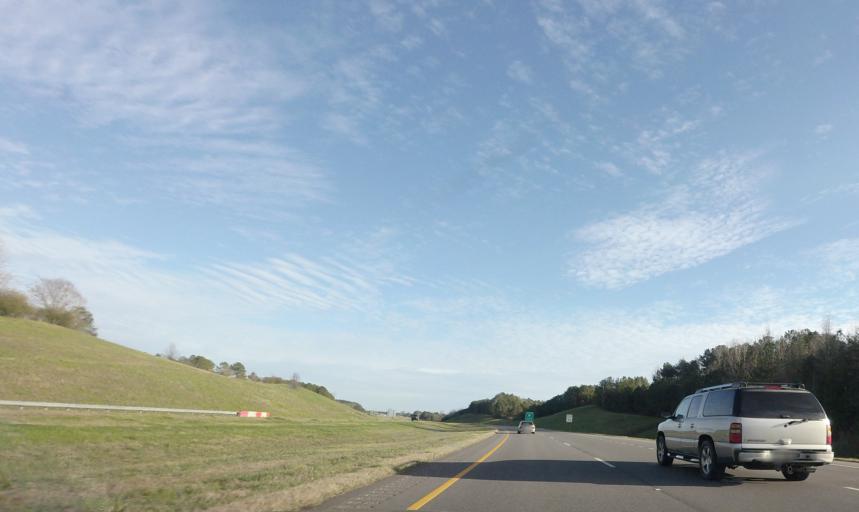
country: US
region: Alabama
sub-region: Walker County
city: Jasper
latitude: 33.8139
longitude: -87.3085
